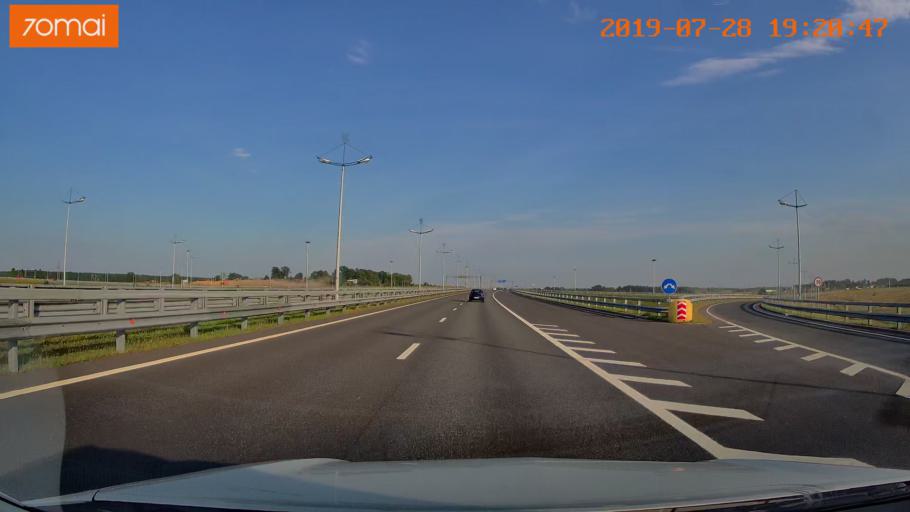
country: RU
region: Kaliningrad
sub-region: Zelenogradskiy Rayon
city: Zelenogradsk
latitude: 54.9120
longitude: 20.4943
